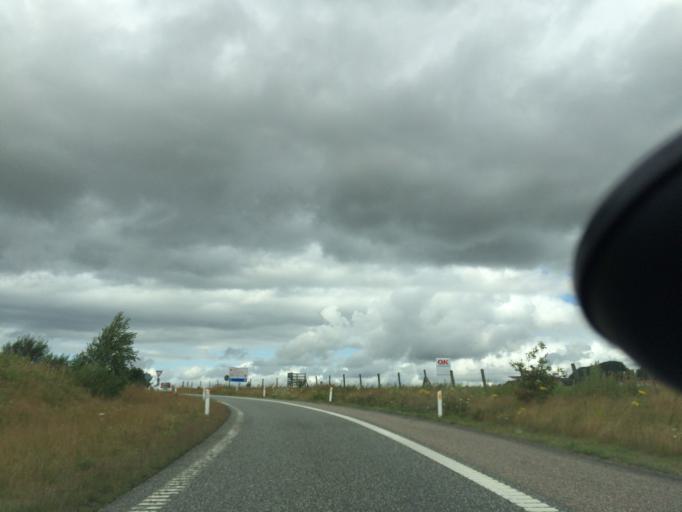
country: DK
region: Central Jutland
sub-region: Skanderborg Kommune
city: Galten
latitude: 56.1453
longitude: 9.9200
